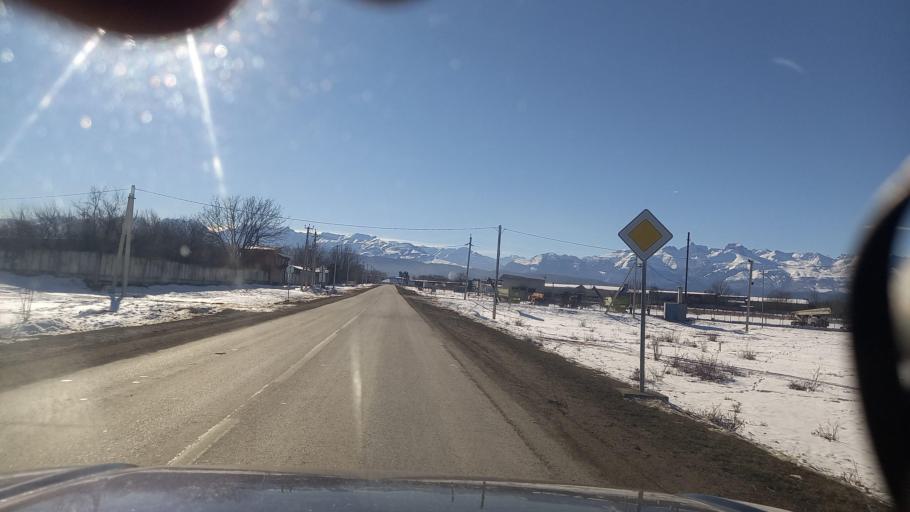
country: RU
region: North Ossetia
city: Chikola
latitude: 43.2098
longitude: 43.9209
